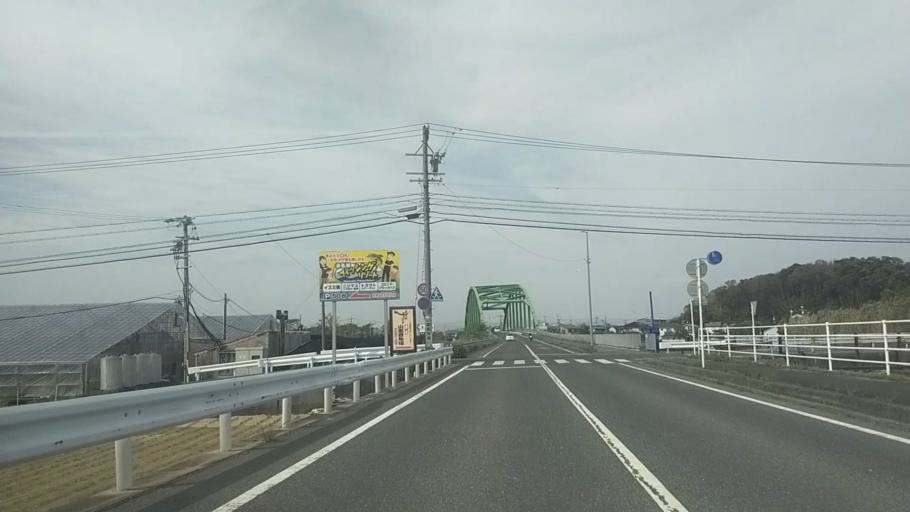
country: JP
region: Shizuoka
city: Kosai-shi
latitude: 34.7085
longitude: 137.6181
